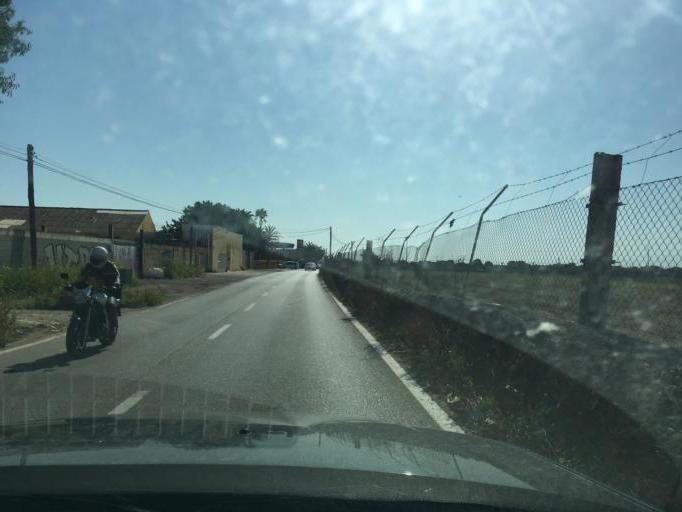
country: ES
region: Balearic Islands
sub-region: Illes Balears
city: Palma
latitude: 39.5775
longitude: 2.6847
